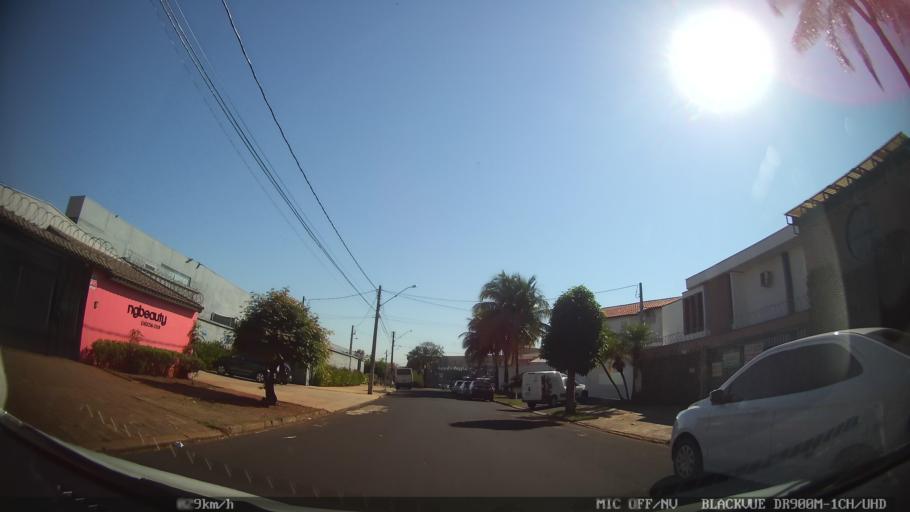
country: BR
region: Sao Paulo
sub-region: Ribeirao Preto
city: Ribeirao Preto
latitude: -21.1989
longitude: -47.8142
